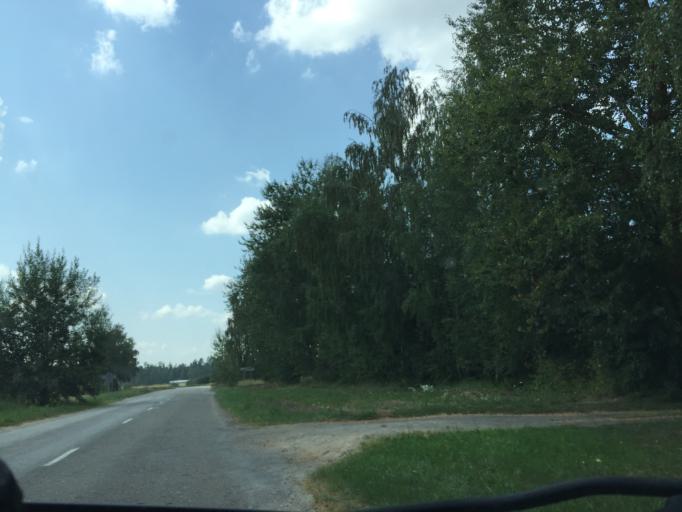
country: LV
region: Tervete
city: Zelmeni
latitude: 56.4028
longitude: 23.3258
